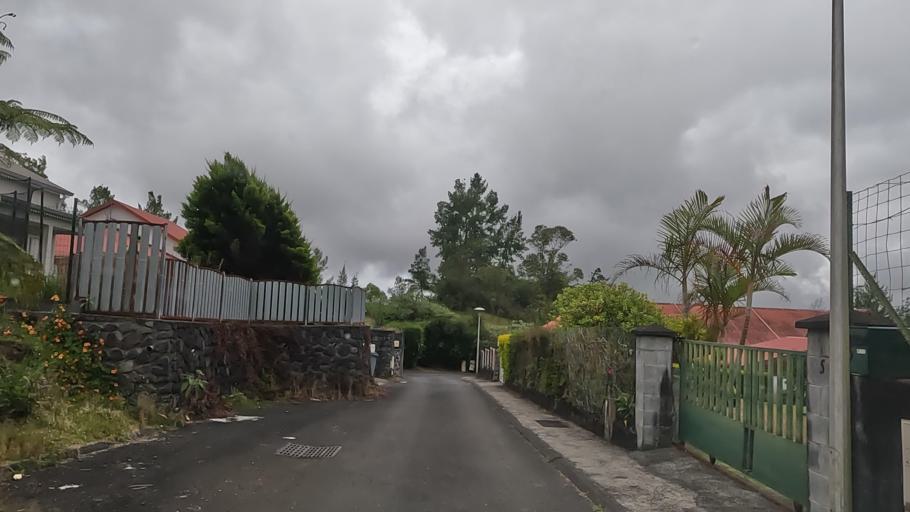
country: RE
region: Reunion
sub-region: Reunion
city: Saint-Benoit
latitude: -21.1389
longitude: 55.6264
